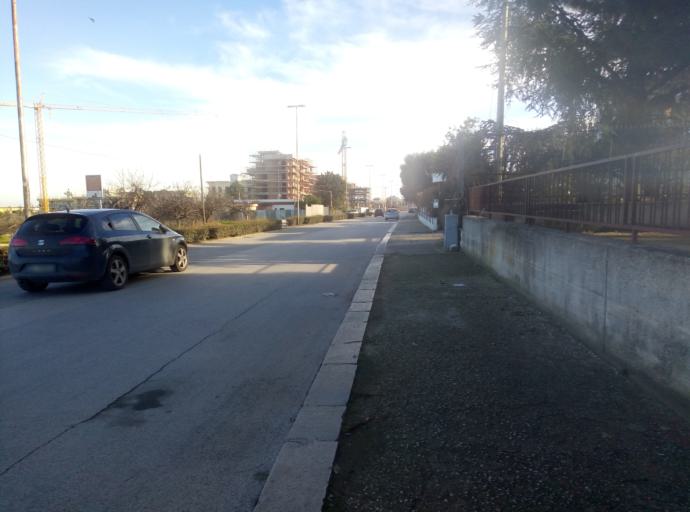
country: IT
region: Apulia
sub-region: Provincia di Bari
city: Ruvo di Puglia
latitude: 41.1216
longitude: 16.4904
